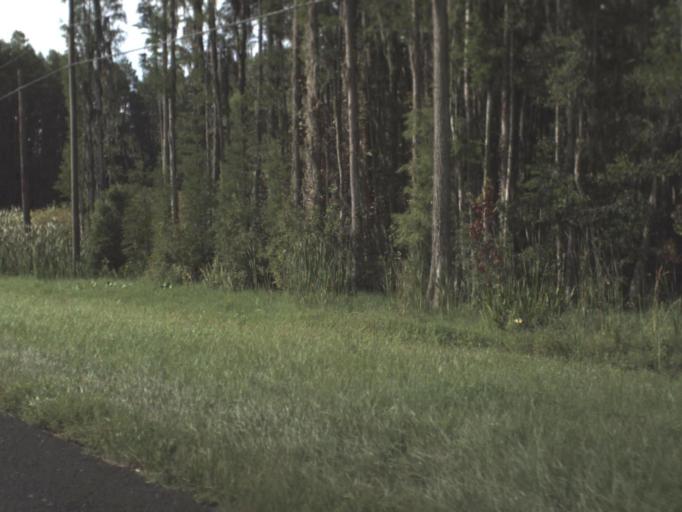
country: US
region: Florida
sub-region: Pasco County
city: Land O' Lakes
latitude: 28.2530
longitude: -82.4692
